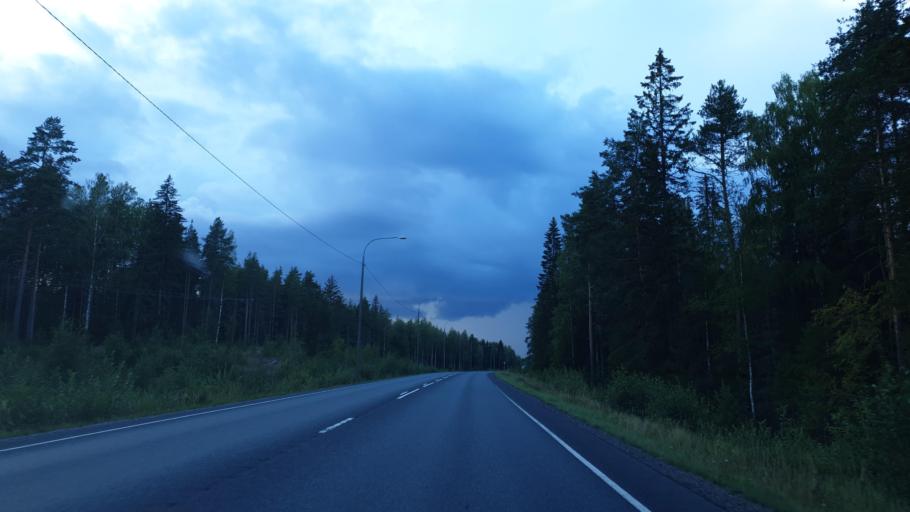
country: FI
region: Northern Savo
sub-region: Varkaus
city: Leppaevirta
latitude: 62.5257
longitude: 27.6663
